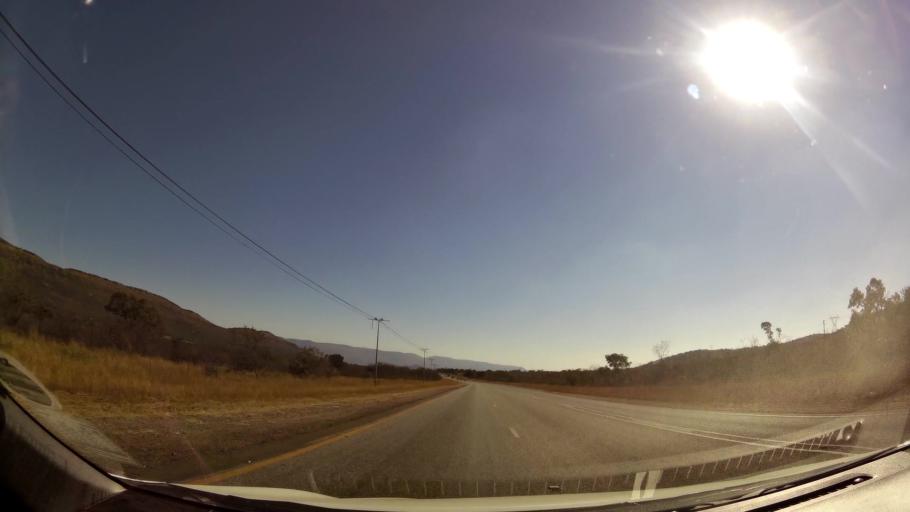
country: ZA
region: Limpopo
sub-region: Waterberg District Municipality
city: Mokopane
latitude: -24.1650
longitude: 29.0735
